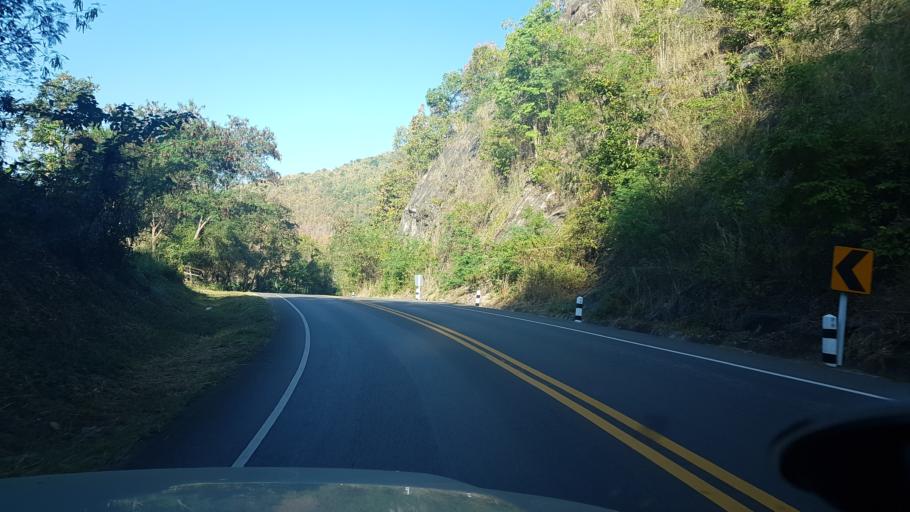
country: TH
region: Phetchabun
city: Lom Sak
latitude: 16.7461
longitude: 101.3997
